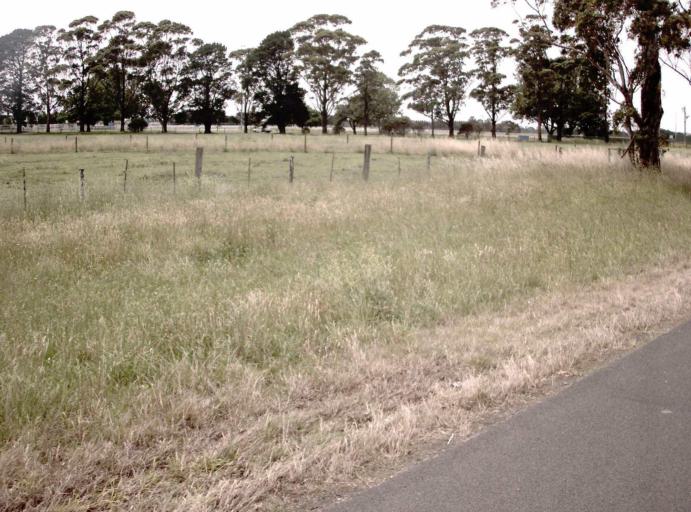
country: AU
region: Victoria
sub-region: Wellington
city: Sale
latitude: -38.0700
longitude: 147.0365
